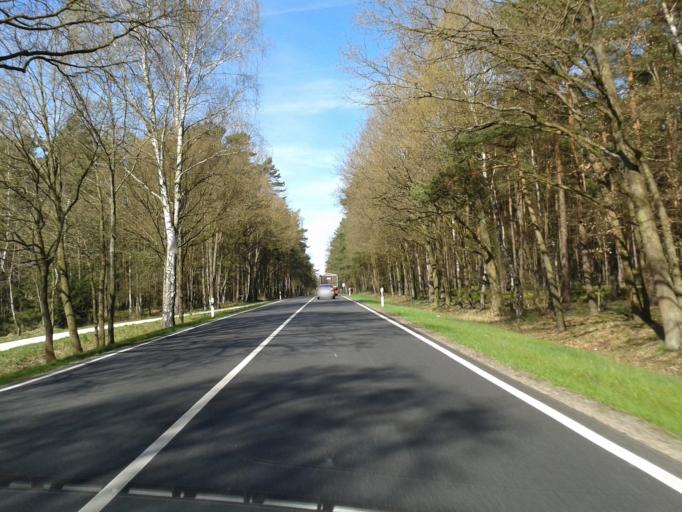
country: DE
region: Lower Saxony
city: Schnega
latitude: 52.9258
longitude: 10.8456
